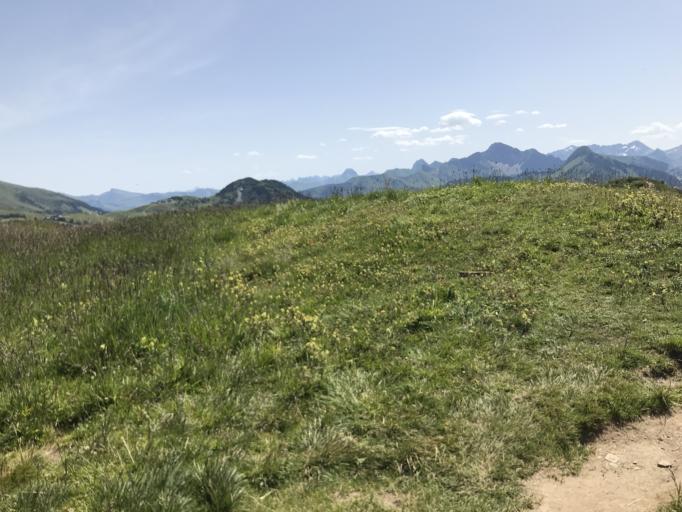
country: AT
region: Vorarlberg
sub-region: Politischer Bezirk Bregenz
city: Damuels
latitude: 47.2923
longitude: 9.8541
